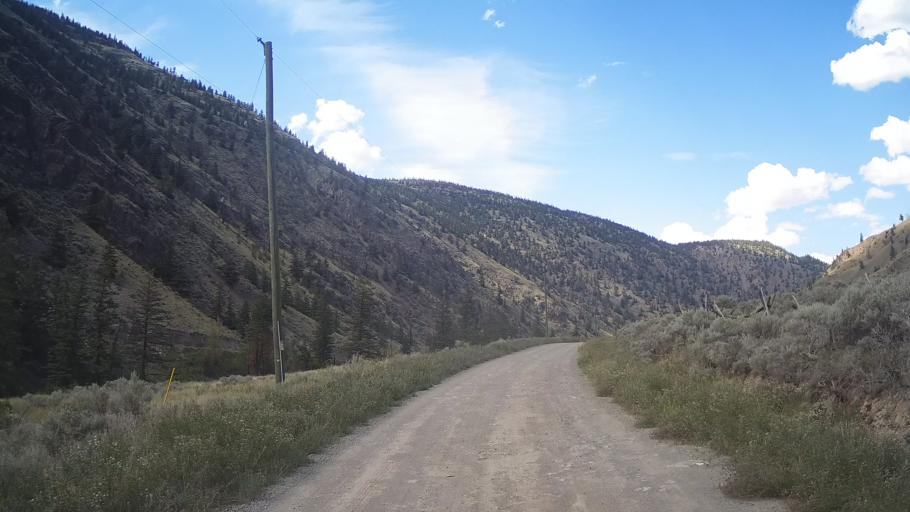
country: CA
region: British Columbia
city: Lillooet
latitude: 51.2038
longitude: -122.0983
